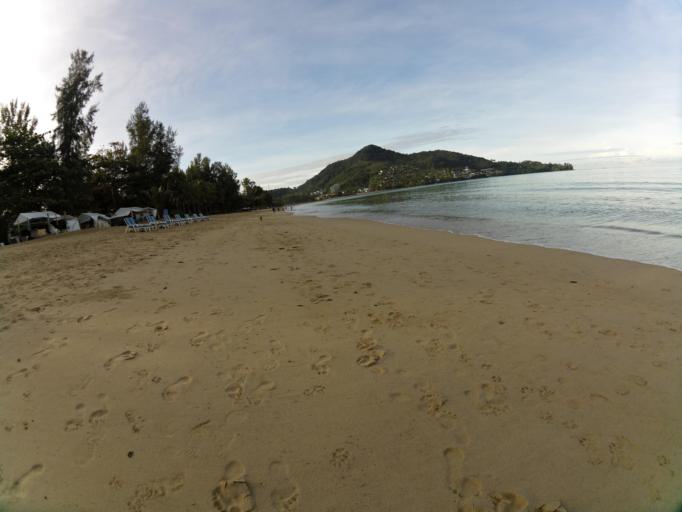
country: TH
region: Phuket
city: Patong
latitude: 7.9589
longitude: 98.2835
